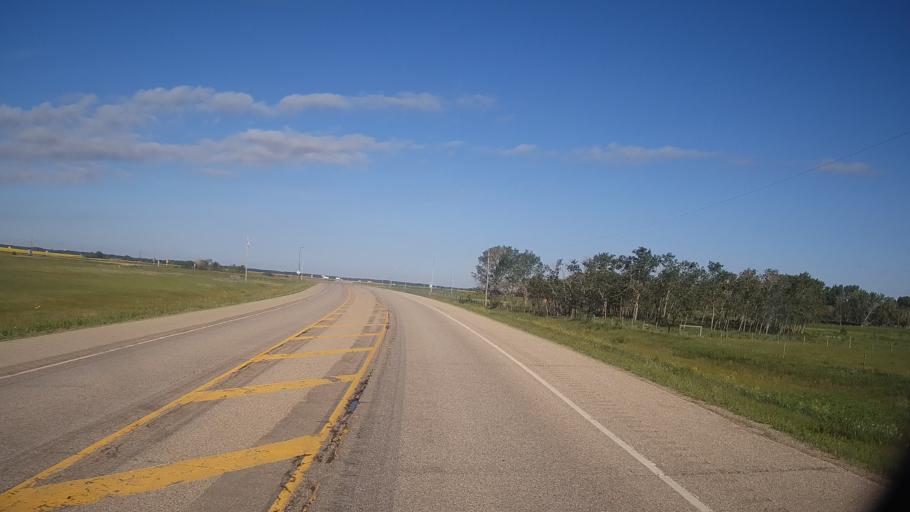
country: CA
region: Saskatchewan
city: Lanigan
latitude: 51.8755
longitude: -105.1880
